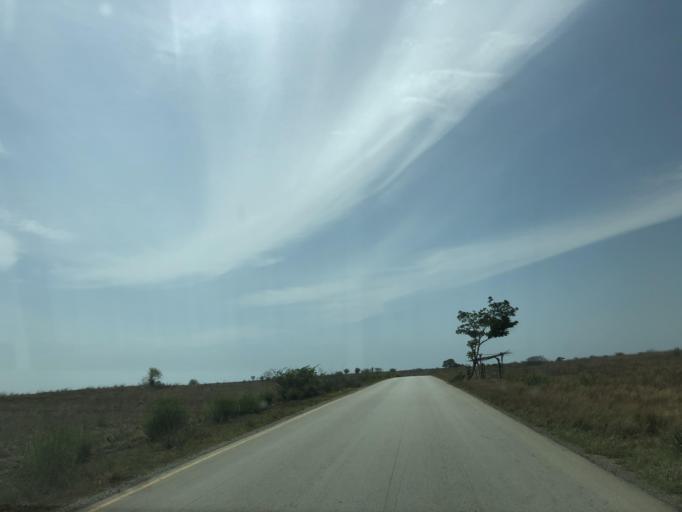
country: AO
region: Cuanza Sul
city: Sumbe
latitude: -10.3597
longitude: 13.6417
